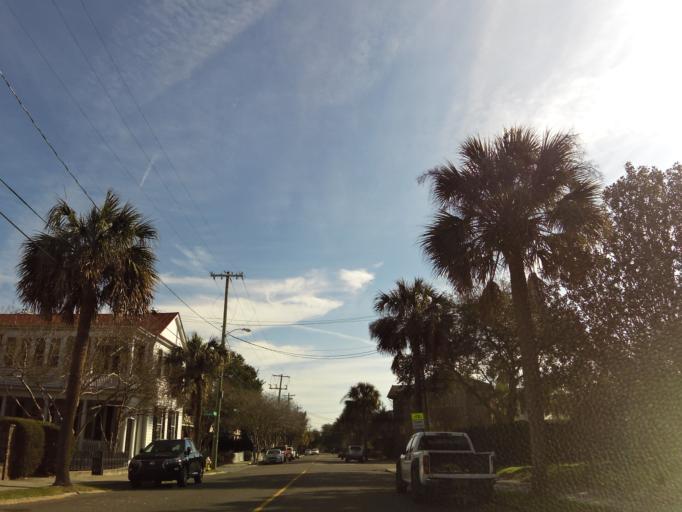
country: US
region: South Carolina
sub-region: Charleston County
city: Charleston
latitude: 32.7734
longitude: -79.9425
